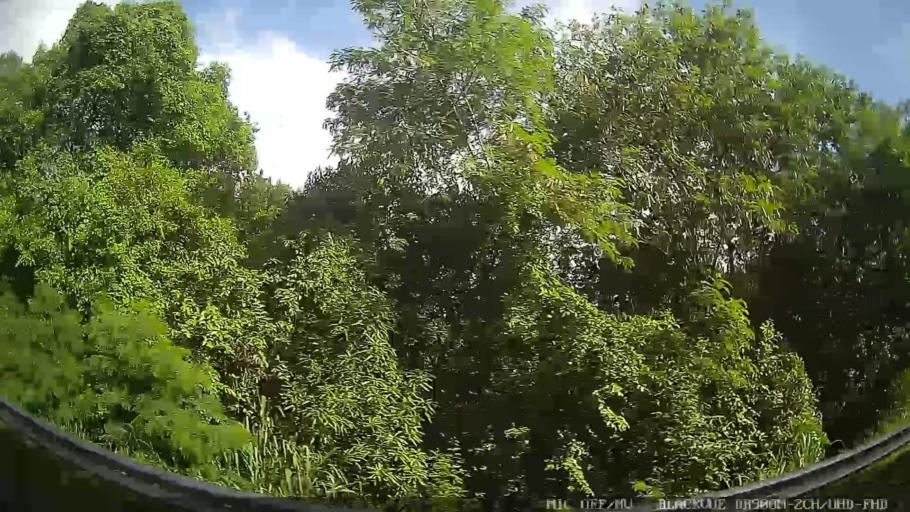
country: BR
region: Sao Paulo
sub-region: Tiete
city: Tiete
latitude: -23.0887
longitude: -47.6823
